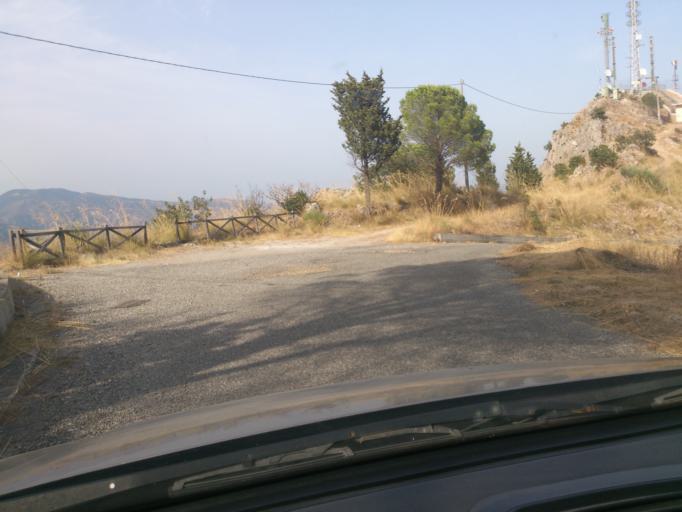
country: IT
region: Calabria
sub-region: Provincia di Reggio Calabria
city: Pazzano
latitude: 38.4709
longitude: 16.4503
